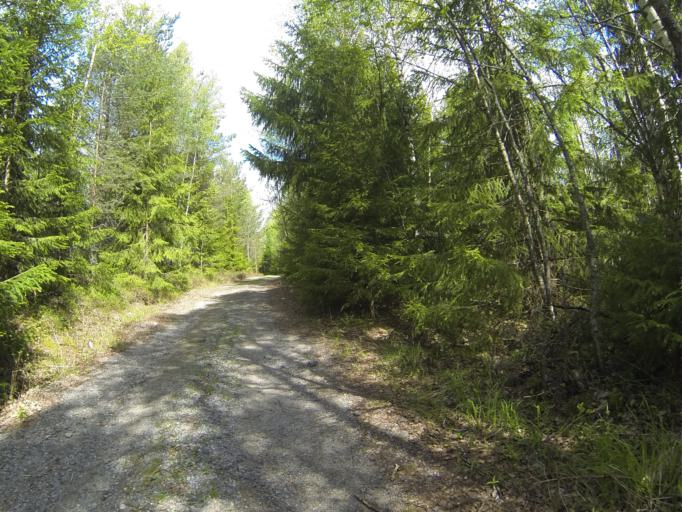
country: FI
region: Varsinais-Suomi
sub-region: Salo
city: Halikko
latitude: 60.3054
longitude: 23.0752
